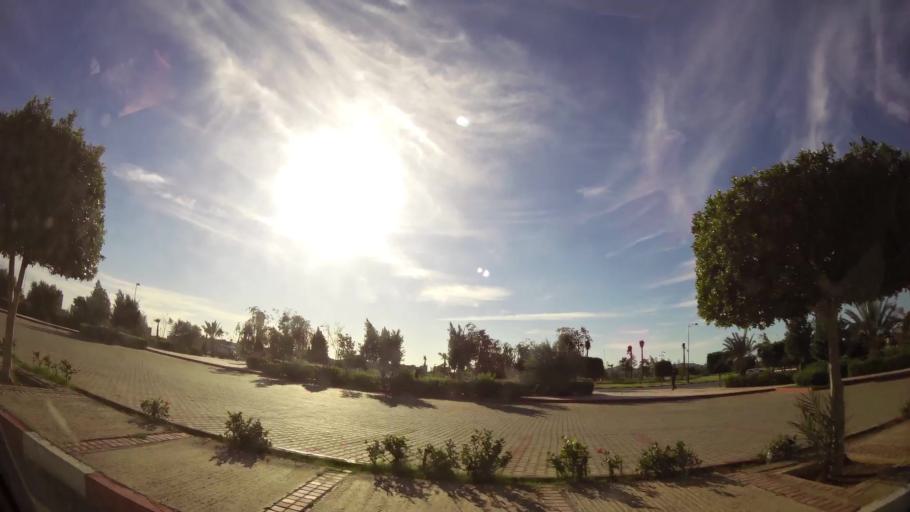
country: MA
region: Marrakech-Tensift-Al Haouz
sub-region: Marrakech
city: Marrakesh
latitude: 31.7537
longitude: -8.1099
